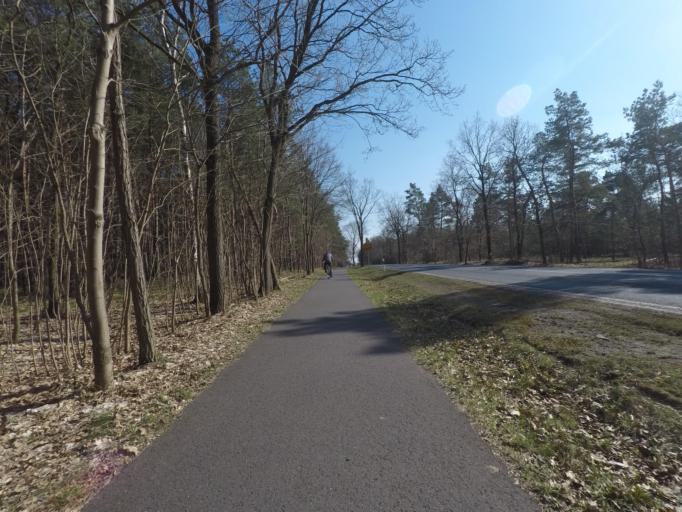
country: DE
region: Brandenburg
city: Britz
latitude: 52.8576
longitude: 13.7586
